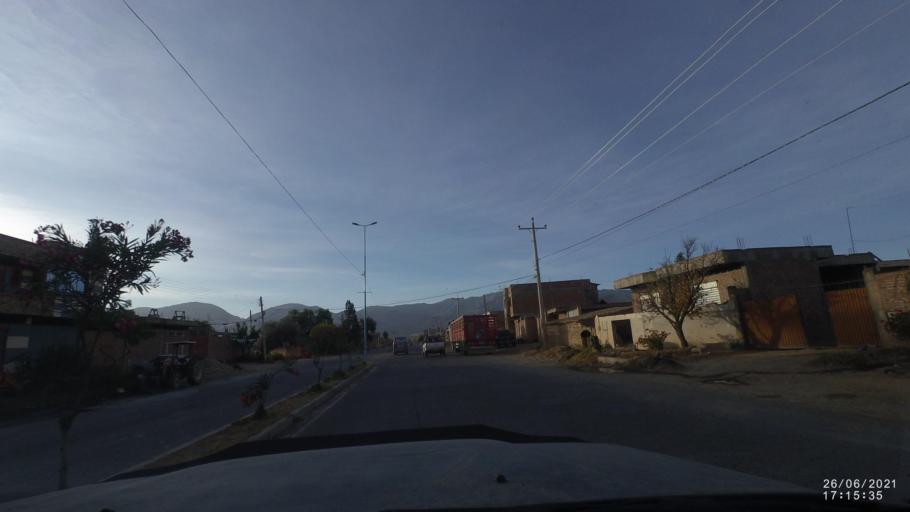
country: BO
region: Cochabamba
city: Cliza
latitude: -17.5703
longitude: -65.9351
